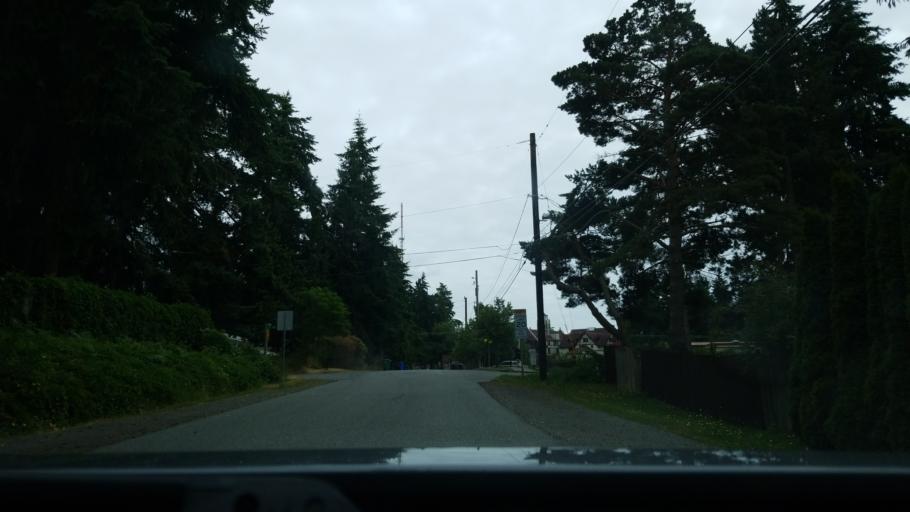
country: US
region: Washington
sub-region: Snohomish County
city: Esperance
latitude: 47.7727
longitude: -122.3536
